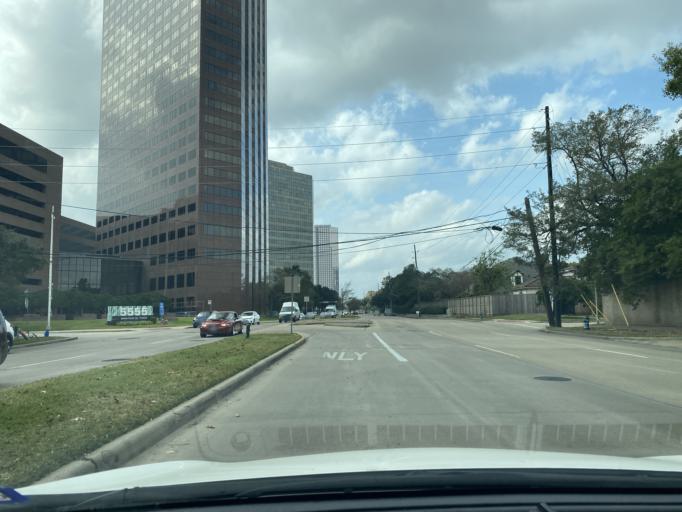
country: US
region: Texas
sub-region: Harris County
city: Hunters Creek Village
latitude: 29.7502
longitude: -95.4704
